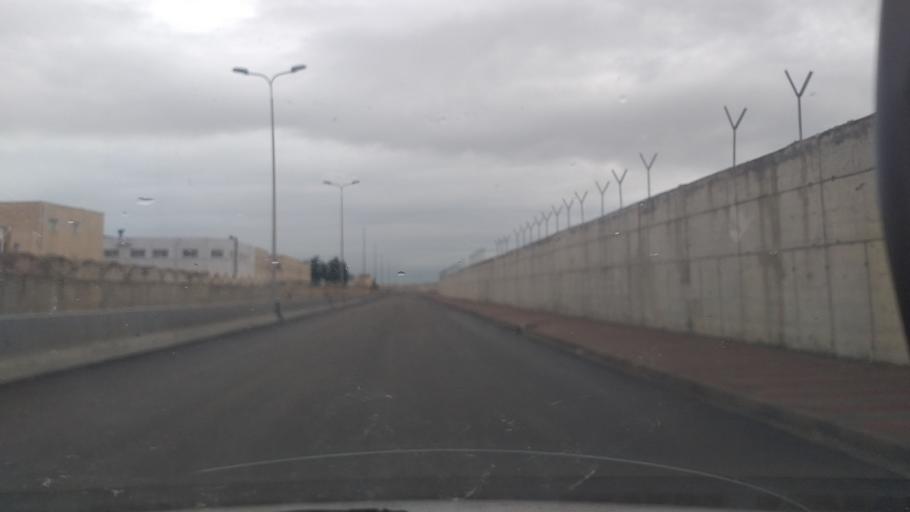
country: TN
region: Ariana
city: Ariana
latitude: 36.8641
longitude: 10.2233
